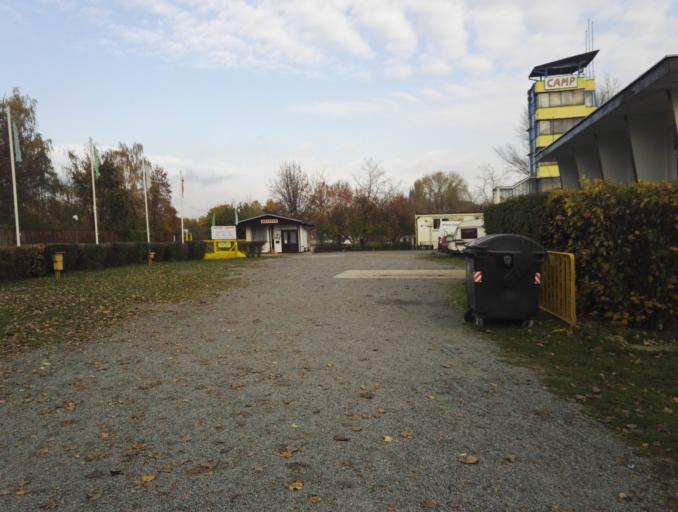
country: CZ
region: Praha
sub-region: Praha 2
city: Vysehrad
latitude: 50.0554
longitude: 14.4132
